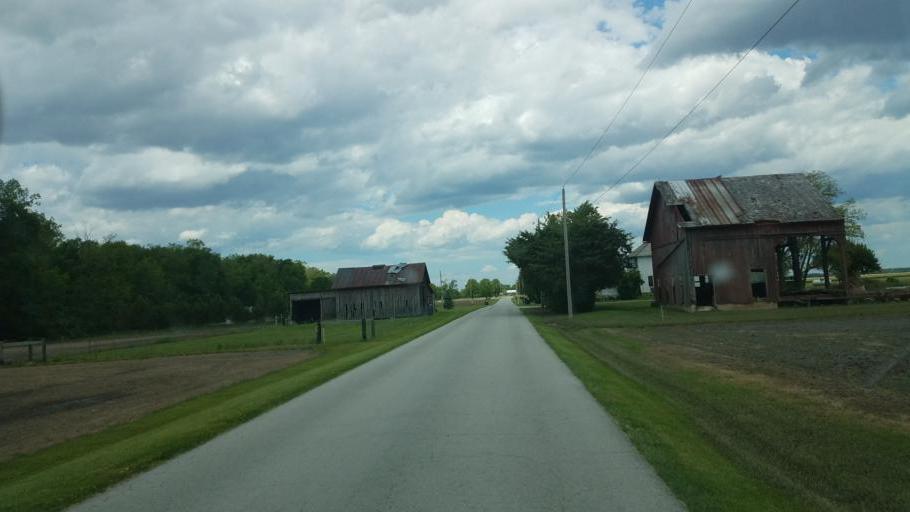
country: US
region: Ohio
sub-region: Huron County
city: Monroeville
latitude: 41.2663
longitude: -82.6783
